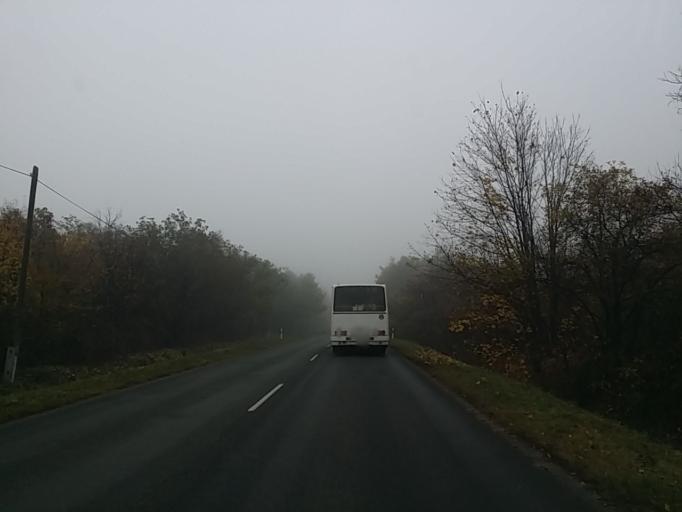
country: HU
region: Heves
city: Gyongyossolymos
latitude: 47.8179
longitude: 19.9605
